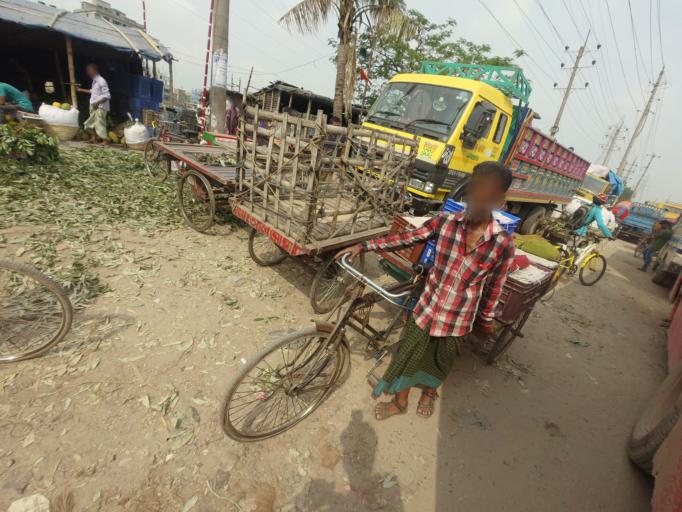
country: BD
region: Dhaka
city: Azimpur
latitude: 23.7232
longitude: 90.3734
